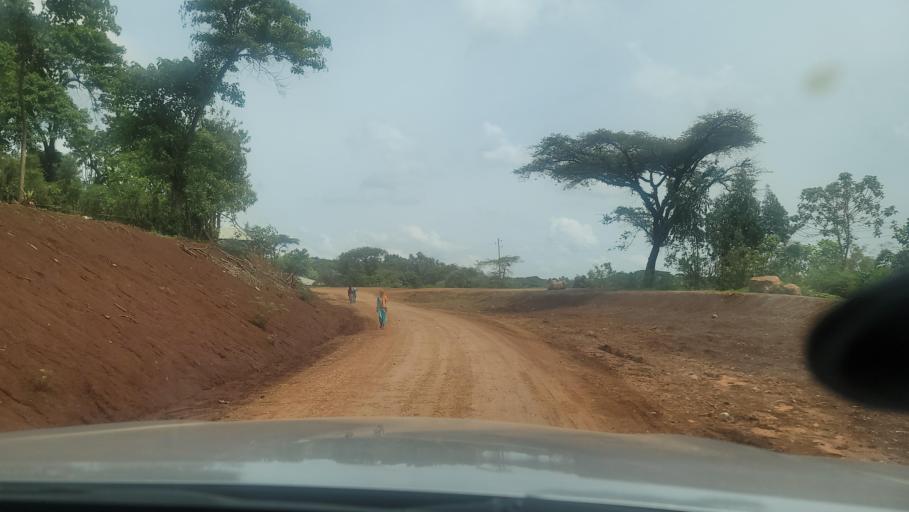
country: ET
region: Oromiya
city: Agaro
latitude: 7.8237
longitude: 36.5333
